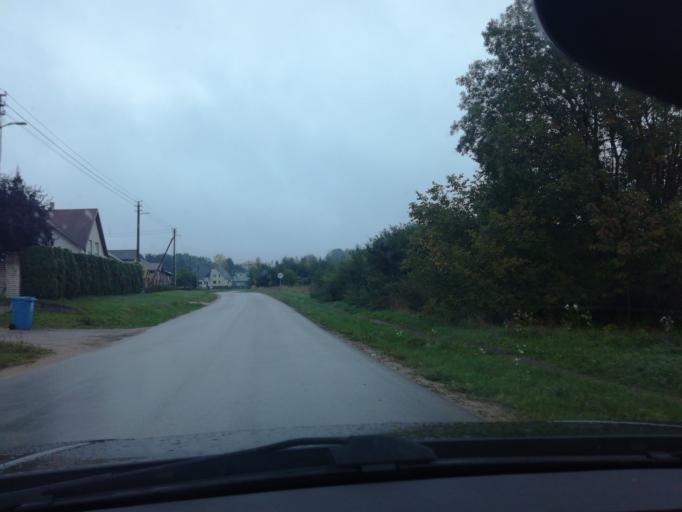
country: LT
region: Alytaus apskritis
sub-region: Alytus
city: Alytus
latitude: 54.3986
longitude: 24.0831
